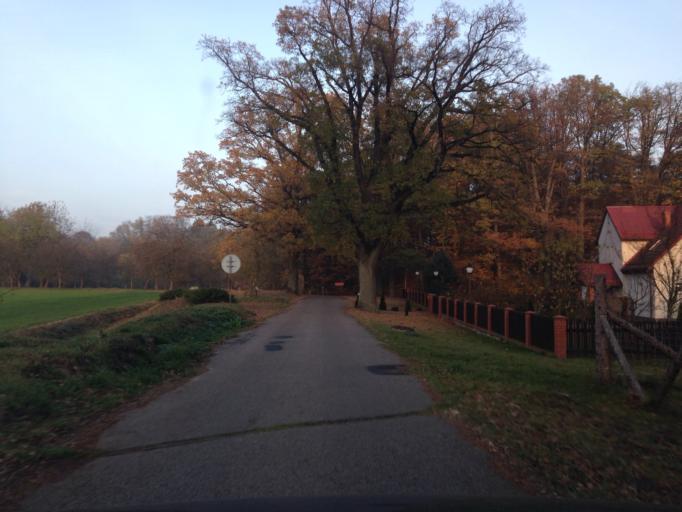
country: PL
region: Warmian-Masurian Voivodeship
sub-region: Powiat dzialdowski
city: Lidzbark
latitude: 53.2488
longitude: 19.7685
